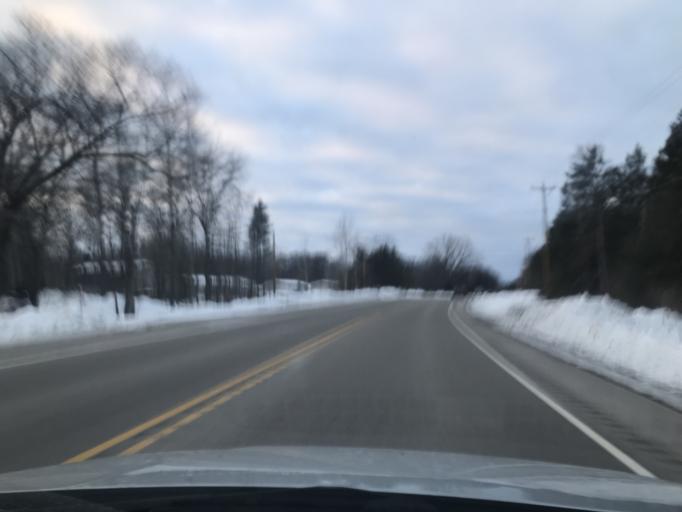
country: US
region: Wisconsin
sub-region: Marinette County
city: Peshtigo
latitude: 45.1614
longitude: -87.7234
